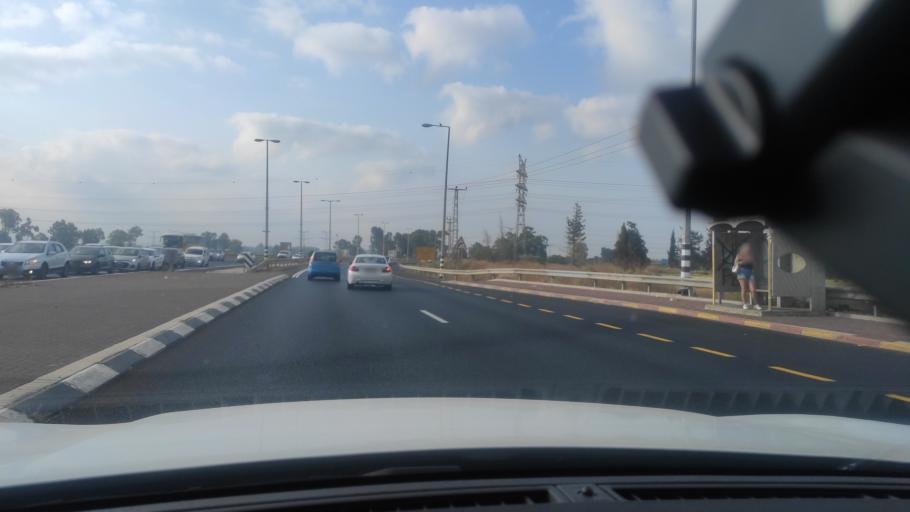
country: IL
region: Central District
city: Hod HaSharon
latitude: 32.1290
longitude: 34.9027
